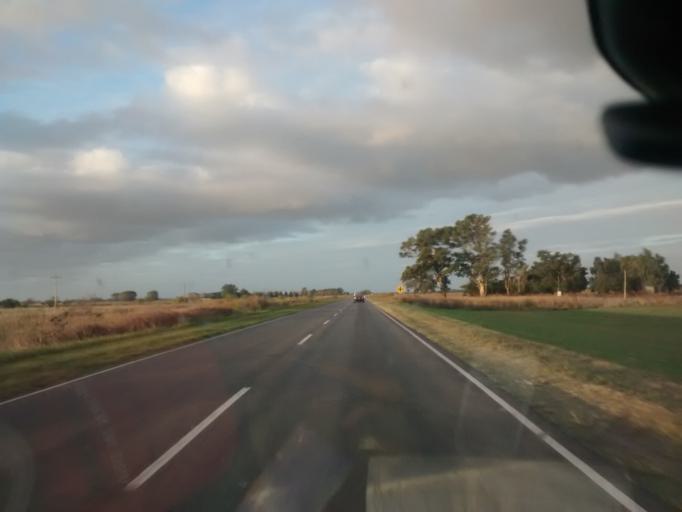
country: AR
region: Buenos Aires
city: Ranchos
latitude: -35.5550
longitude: -58.3924
